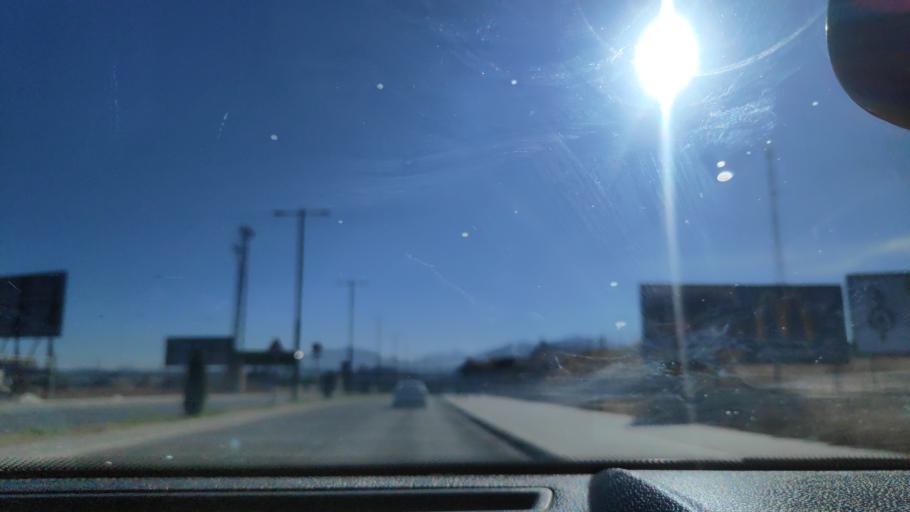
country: ES
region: Andalusia
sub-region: Provincia de Jaen
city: Jaen
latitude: 37.7916
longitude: -3.7842
